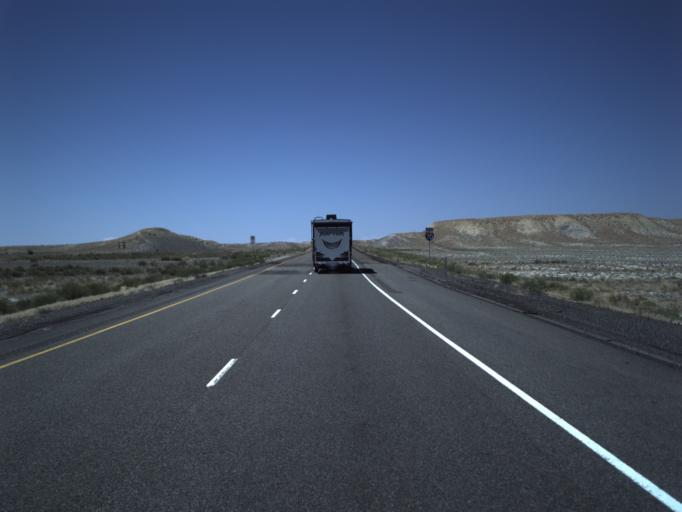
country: US
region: Utah
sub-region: Grand County
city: Moab
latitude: 38.9428
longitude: -109.6241
